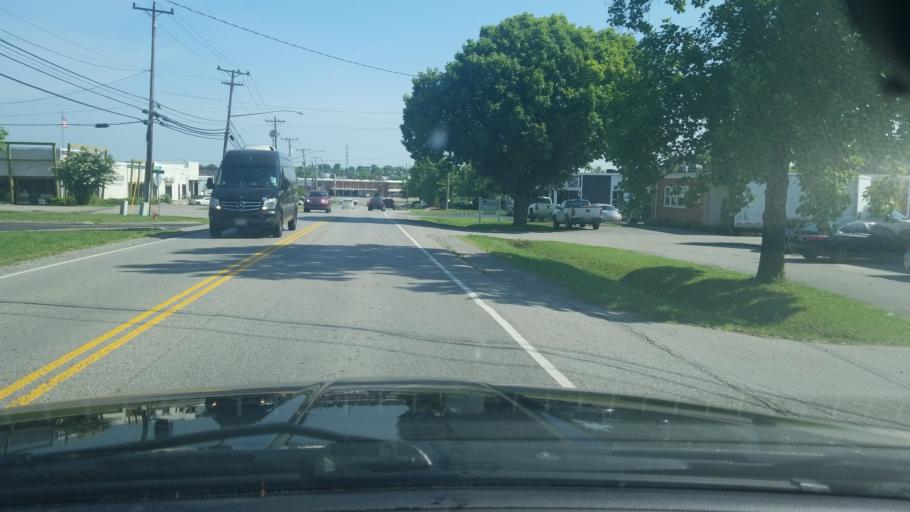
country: US
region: Tennessee
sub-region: Davidson County
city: Oak Hill
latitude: 36.1091
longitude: -86.7555
